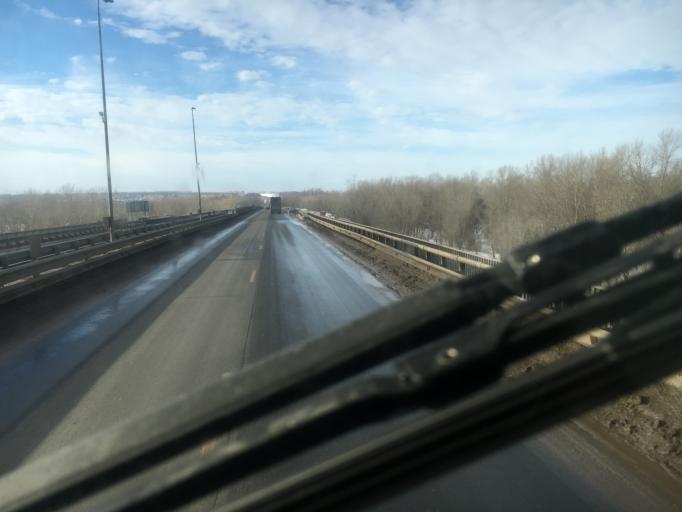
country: RU
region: Samara
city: Mirnyy
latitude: 53.4321
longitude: 50.2985
